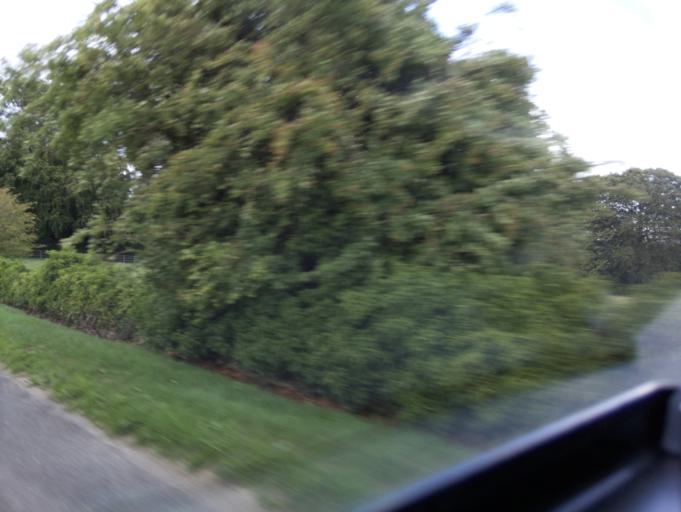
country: GB
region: England
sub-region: Gloucestershire
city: Donnington
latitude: 51.9893
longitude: -1.7535
